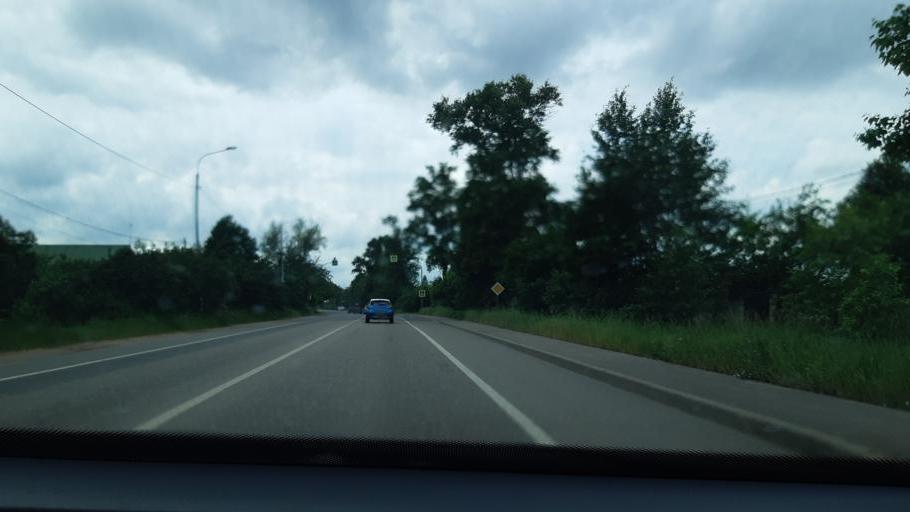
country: RU
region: Moskovskaya
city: Chupryakovo
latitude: 55.5603
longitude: 36.5529
